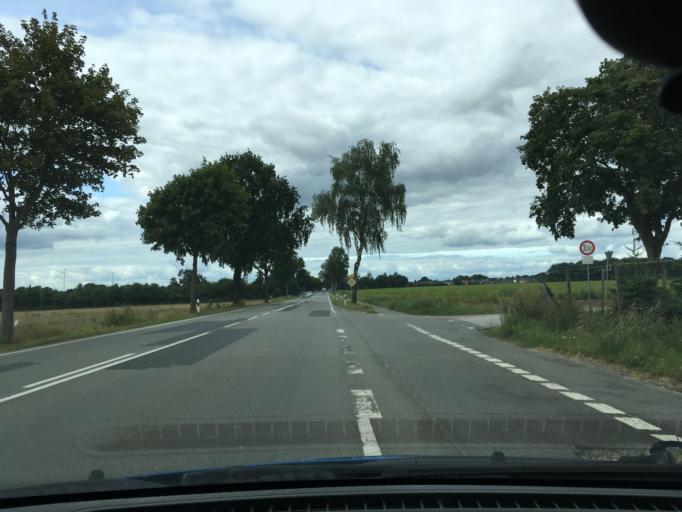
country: DE
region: Lower Saxony
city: Appel
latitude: 53.4146
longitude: 9.7894
